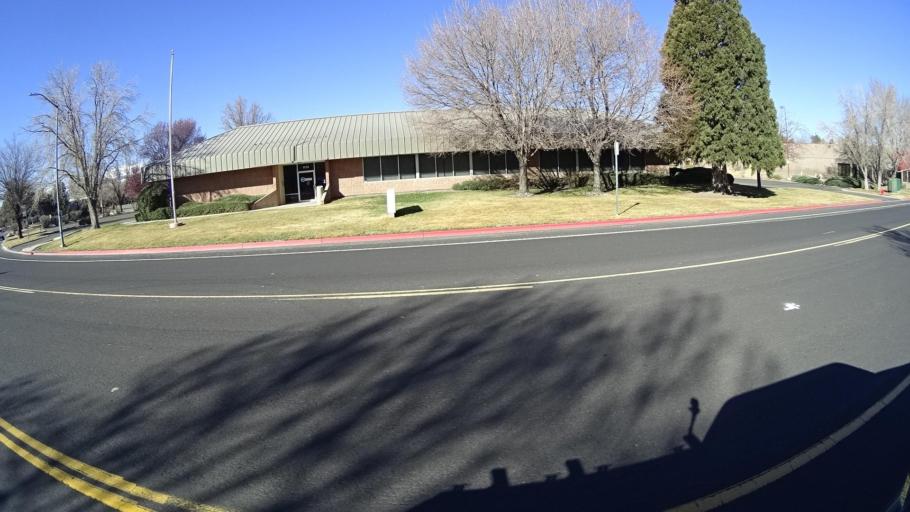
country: US
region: Nevada
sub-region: Washoe County
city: Sparks
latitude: 39.5106
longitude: -119.7471
